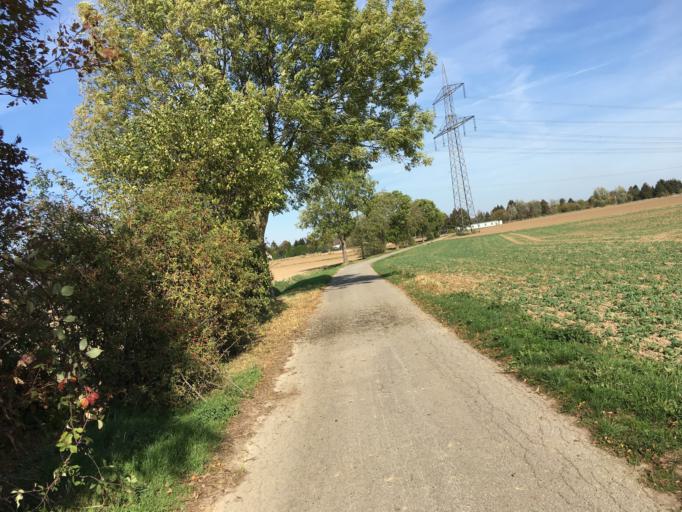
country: DE
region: North Rhine-Westphalia
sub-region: Regierungsbezirk Koln
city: Merzenich
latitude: 50.8613
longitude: 6.5394
